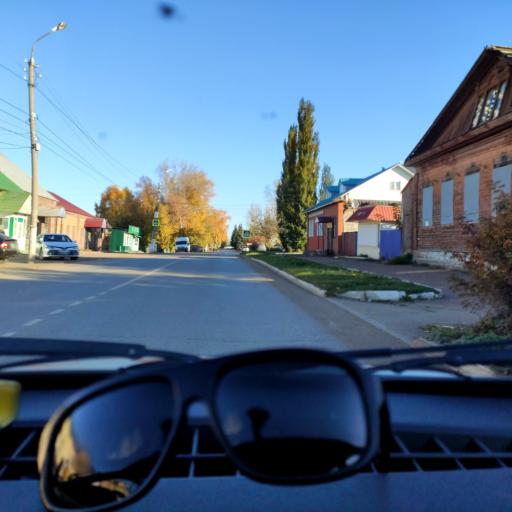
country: RU
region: Bashkortostan
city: Blagoveshchensk
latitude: 55.0280
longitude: 55.9717
